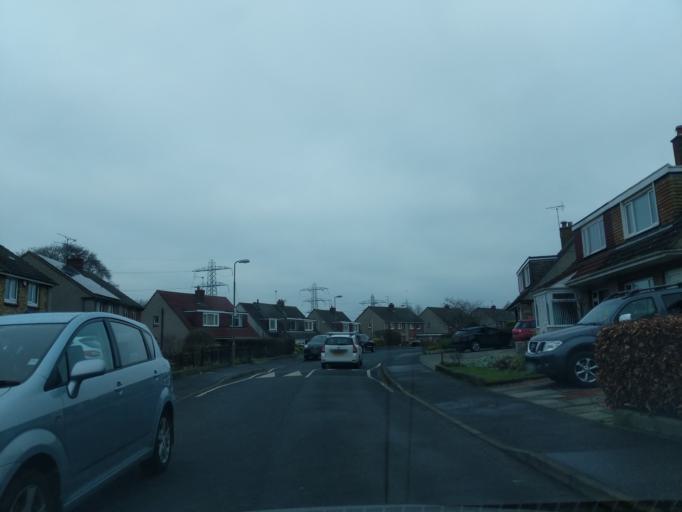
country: GB
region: Scotland
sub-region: Edinburgh
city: Currie
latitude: 55.9006
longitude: -3.3136
